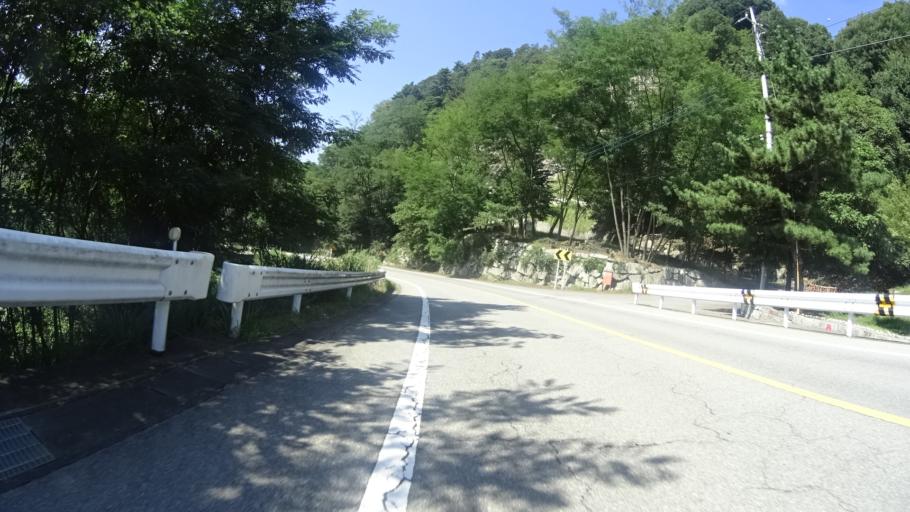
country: JP
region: Yamanashi
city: Enzan
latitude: 35.7381
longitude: 138.8006
